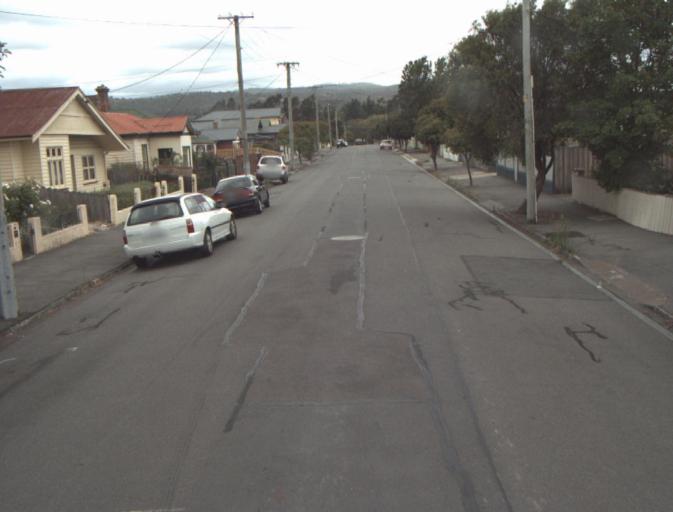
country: AU
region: Tasmania
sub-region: Launceston
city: Newnham
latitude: -41.4171
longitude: 147.1353
